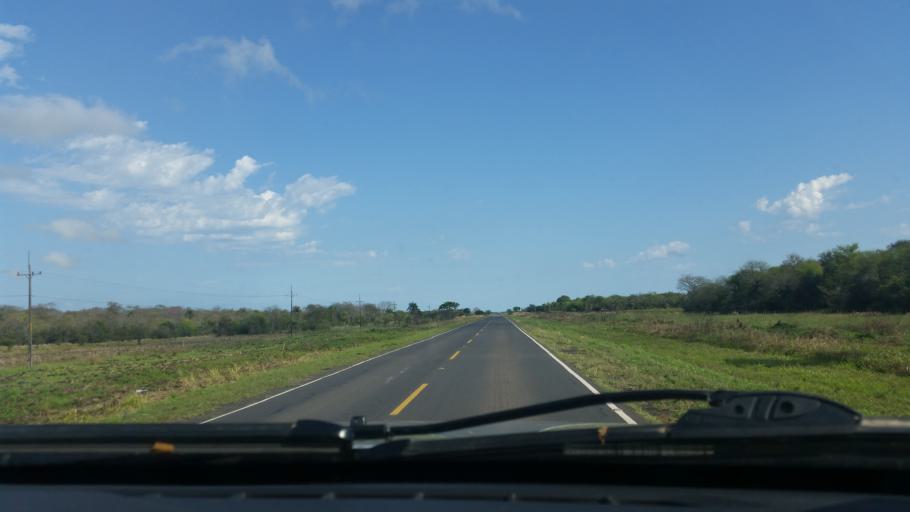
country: PY
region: Presidente Hayes
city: Benjamin Aceval
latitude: -24.9039
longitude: -57.6506
